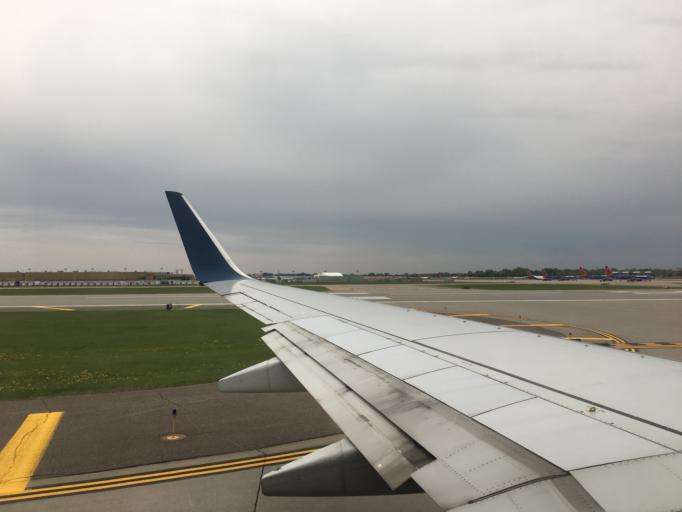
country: US
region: Minnesota
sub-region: Hennepin County
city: Richfield
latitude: 44.8880
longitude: -93.2314
